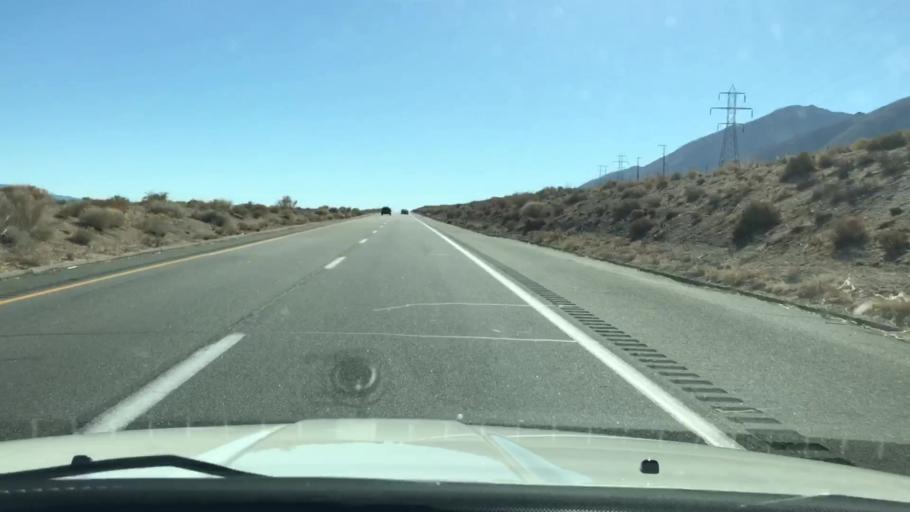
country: US
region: California
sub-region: Inyo County
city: Lone Pine
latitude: 36.4625
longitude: -118.0366
